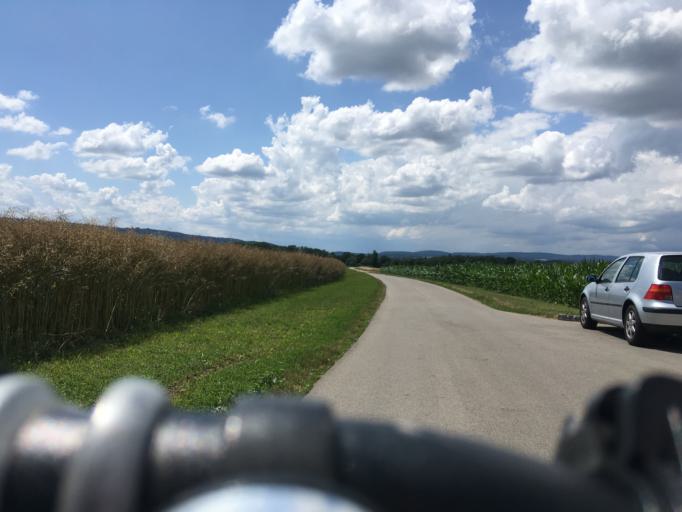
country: CH
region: Thurgau
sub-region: Frauenfeld District
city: Diessenhofen
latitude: 47.6901
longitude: 8.7332
